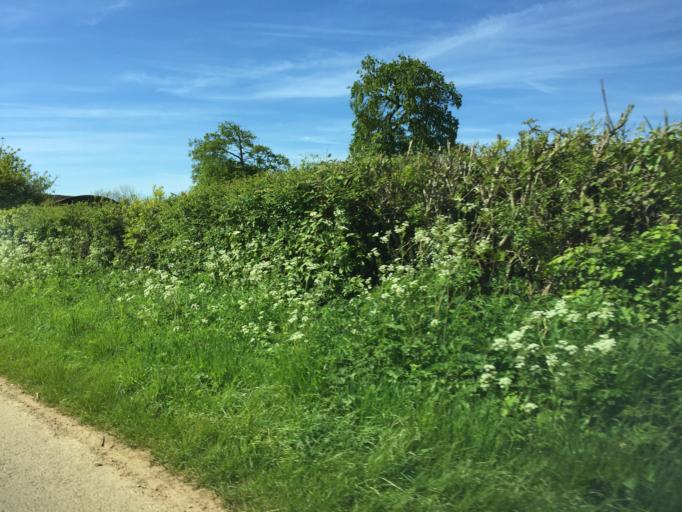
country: GB
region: England
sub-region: Wiltshire
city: Luckington
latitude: 51.5960
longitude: -2.2558
